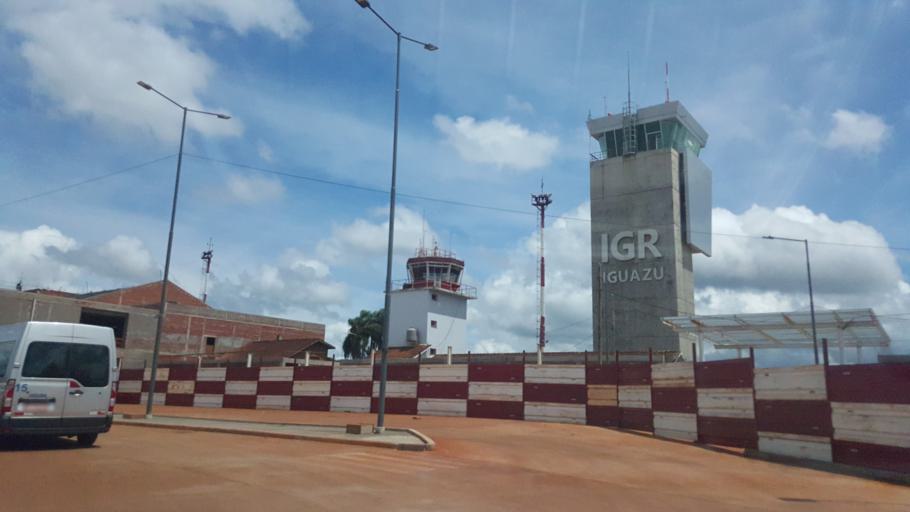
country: AR
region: Misiones
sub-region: Departamento de Iguazu
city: Puerto Iguazu
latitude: -25.7308
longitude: -54.4773
